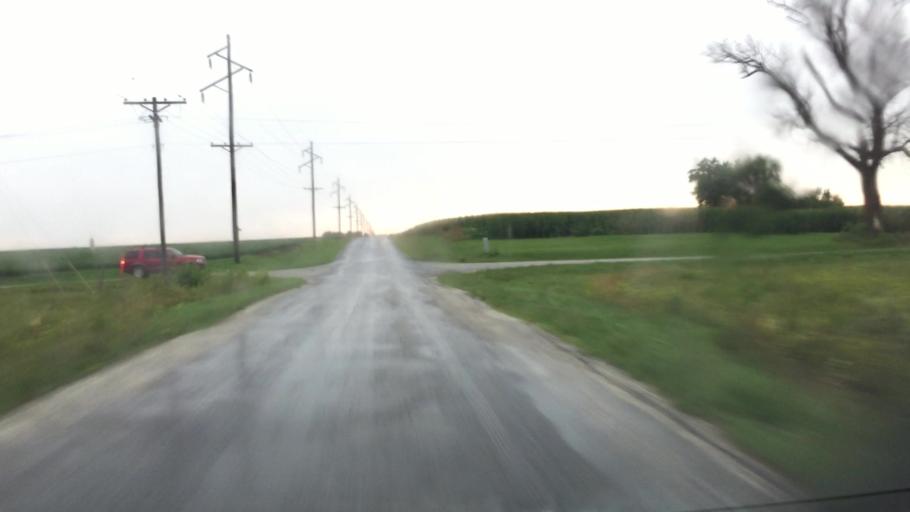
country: US
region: Illinois
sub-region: Hancock County
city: Nauvoo
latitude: 40.5061
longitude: -91.2697
